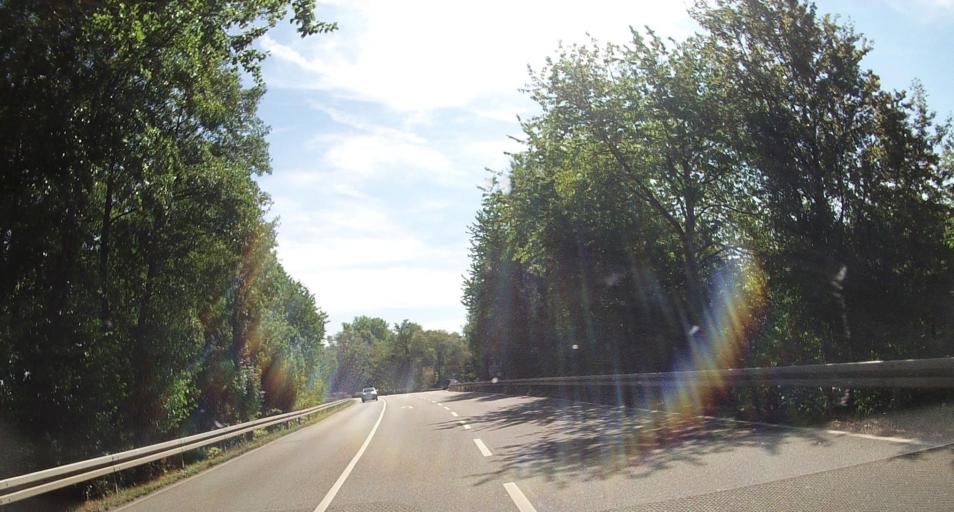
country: DE
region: Baden-Wuerttemberg
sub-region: Karlsruhe Region
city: Rastatt
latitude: 48.8450
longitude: 8.2190
